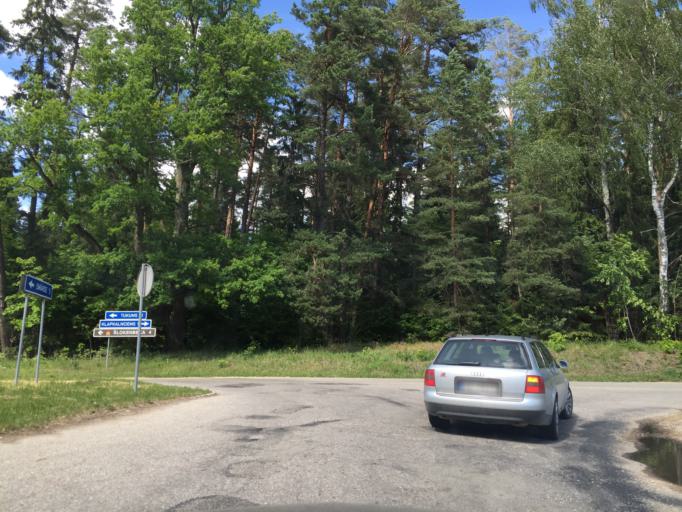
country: LV
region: Engure
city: Smarde
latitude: 56.9839
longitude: 23.2796
